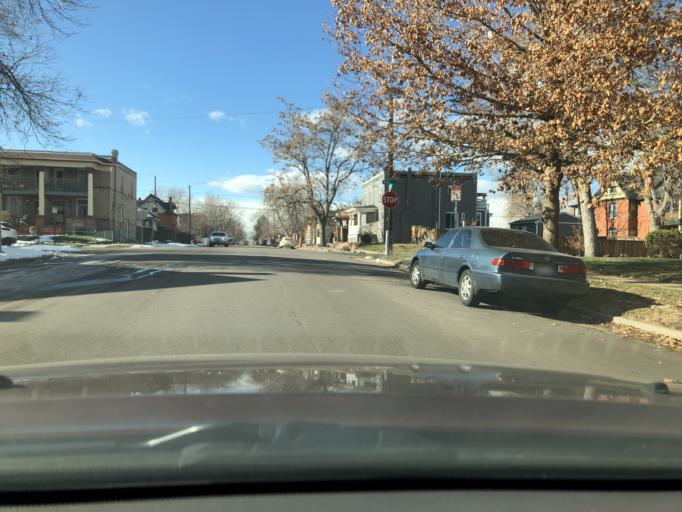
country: US
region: Colorado
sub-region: Denver County
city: Denver
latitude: 39.7532
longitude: -104.9618
